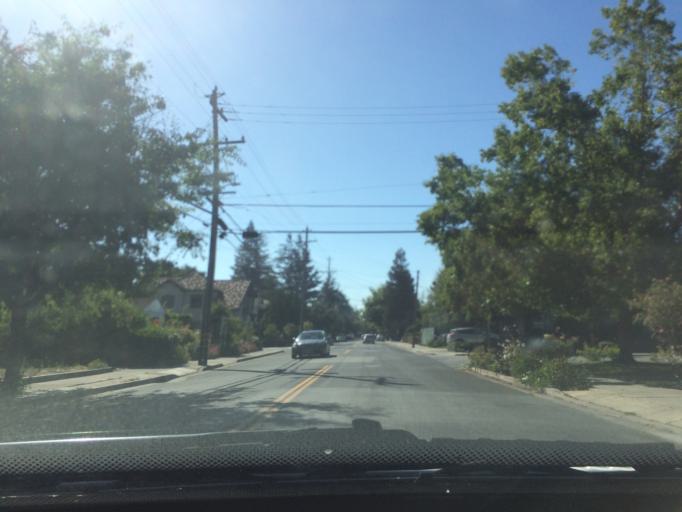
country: US
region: California
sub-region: San Mateo County
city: Menlo Park
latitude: 37.4475
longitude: -122.1829
